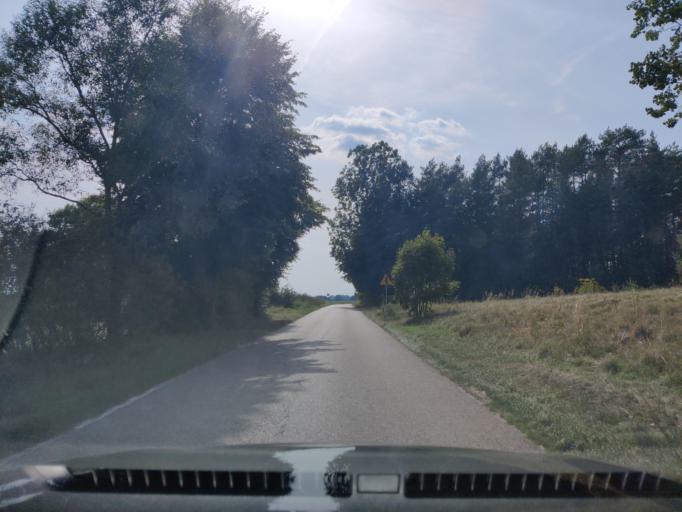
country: PL
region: Masovian Voivodeship
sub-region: Powiat wyszkowski
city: Rzasnik
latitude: 52.7673
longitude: 21.3982
